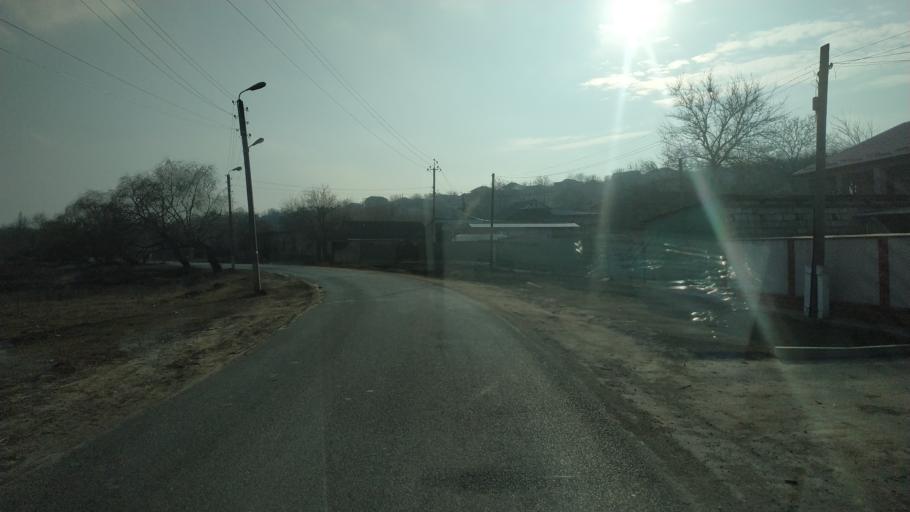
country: MD
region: Hincesti
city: Dancu
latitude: 46.7758
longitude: 28.3464
